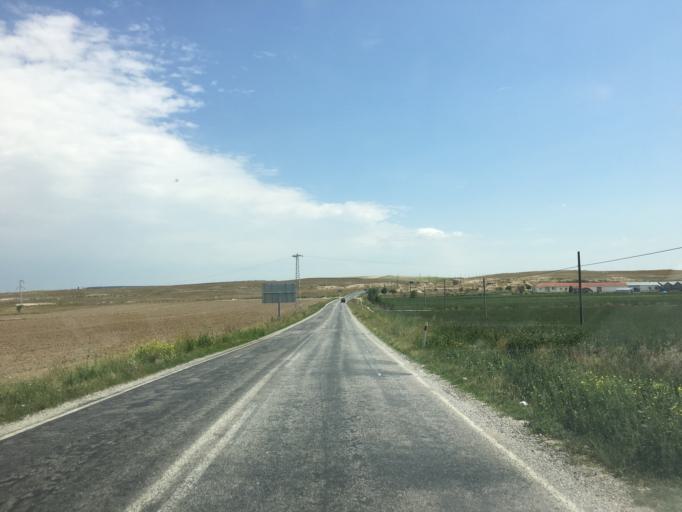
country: TR
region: Eskisehir
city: Cifteler
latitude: 39.3861
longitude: 31.0491
